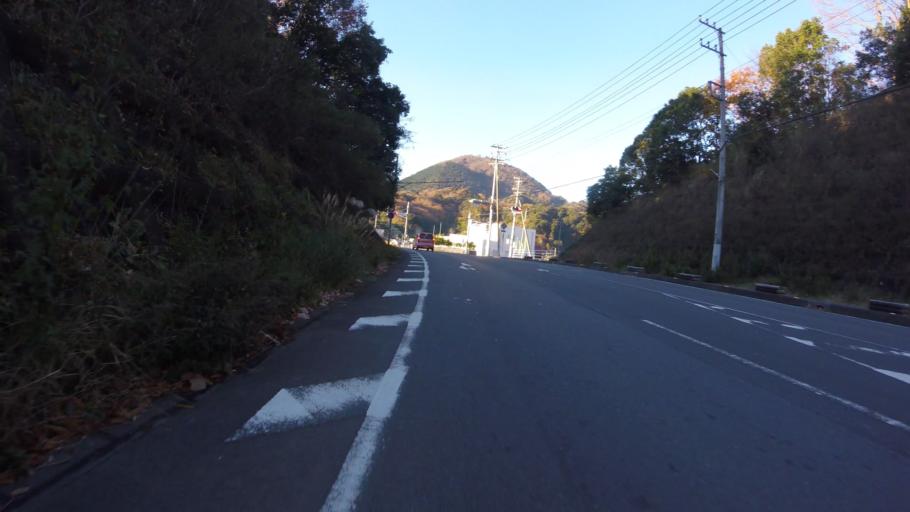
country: JP
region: Shizuoka
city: Mishima
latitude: 35.0213
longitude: 138.9369
